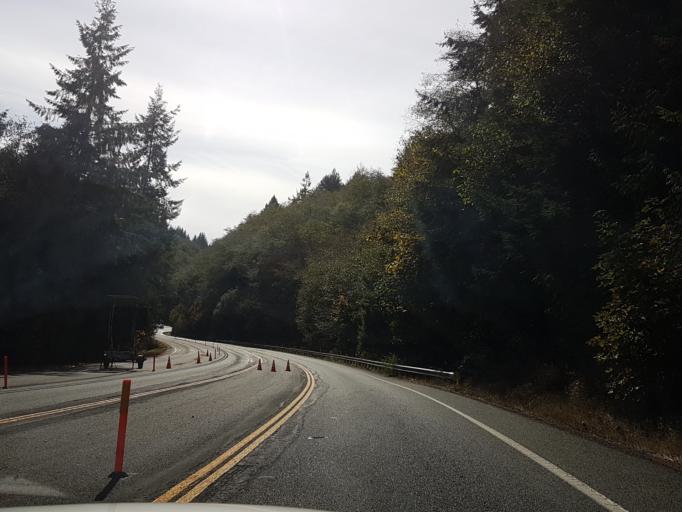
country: US
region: California
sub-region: Del Norte County
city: Bertsch-Oceanview
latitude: 41.4963
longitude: -124.0430
